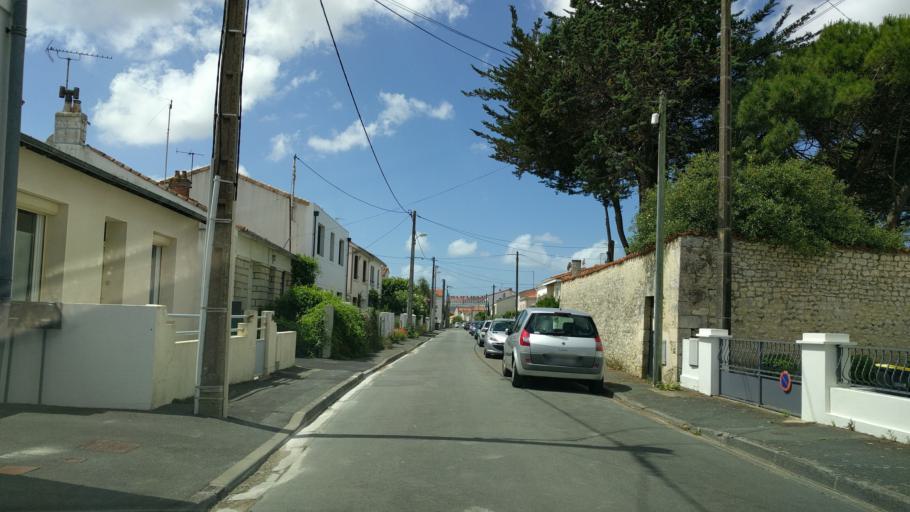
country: FR
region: Poitou-Charentes
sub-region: Departement de la Charente-Maritime
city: La Rochelle
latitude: 46.1733
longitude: -1.1424
